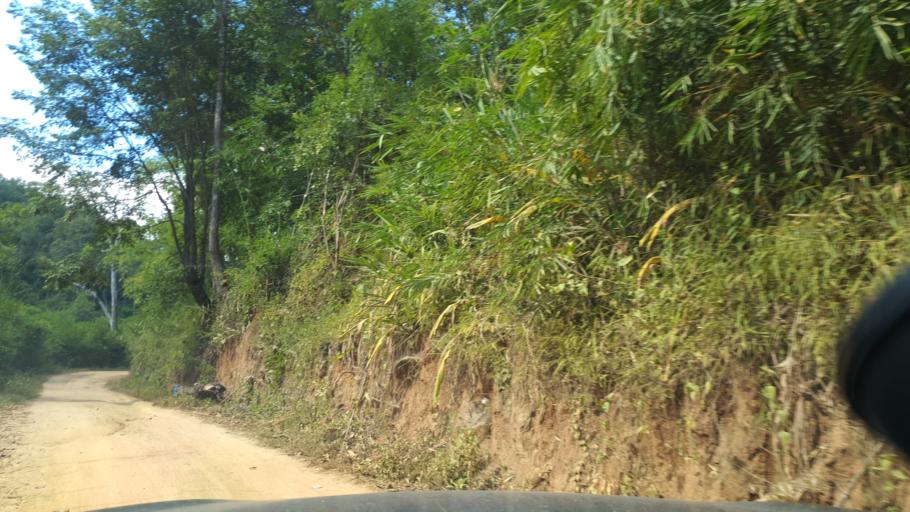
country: TH
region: Chiang Mai
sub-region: Amphoe Chiang Dao
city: Chiang Dao
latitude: 19.2853
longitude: 98.7593
